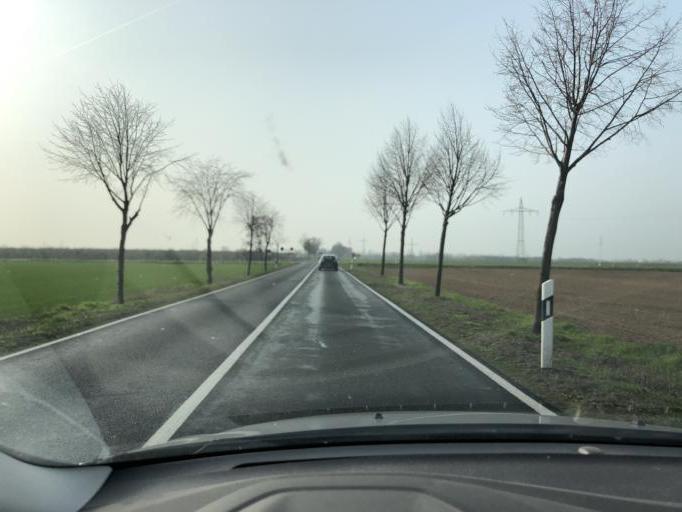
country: DE
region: Saxony-Anhalt
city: Brehna
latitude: 51.5487
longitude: 12.2406
